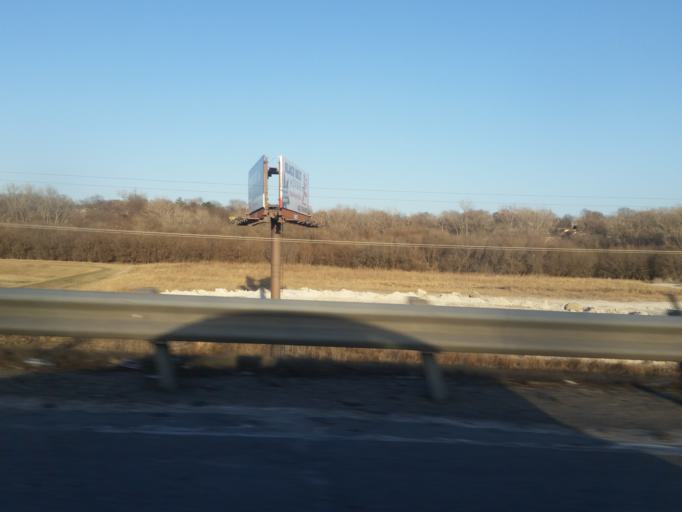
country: US
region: Nebraska
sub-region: Sarpy County
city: Offutt Air Force Base
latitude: 41.1473
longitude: -95.9386
